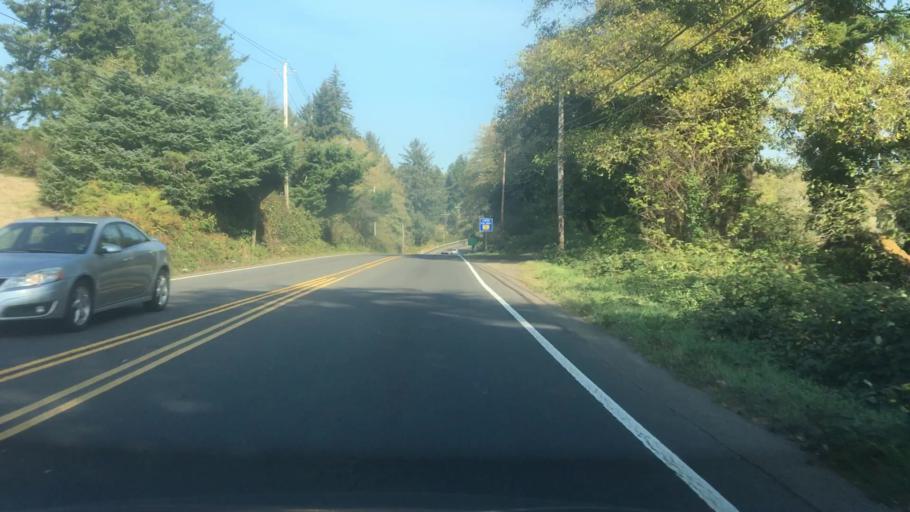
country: US
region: Oregon
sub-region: Lincoln County
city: Lincoln City
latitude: 45.0026
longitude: -123.9858
